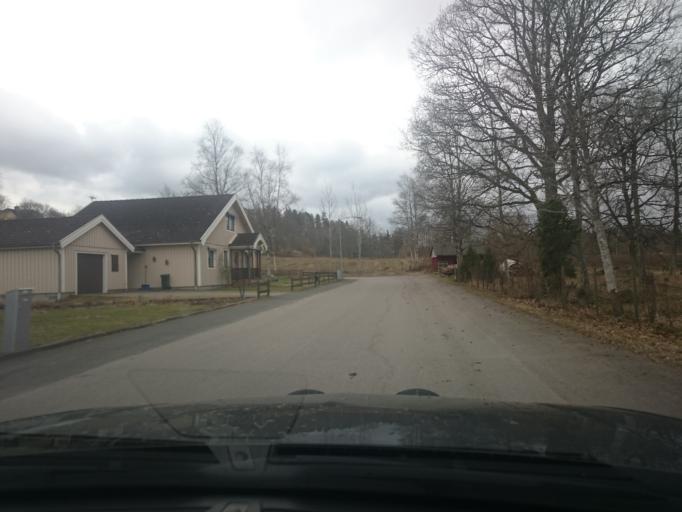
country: SE
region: Joenkoeping
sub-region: Vetlanda Kommun
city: Vetlanda
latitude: 57.2954
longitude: 15.1250
